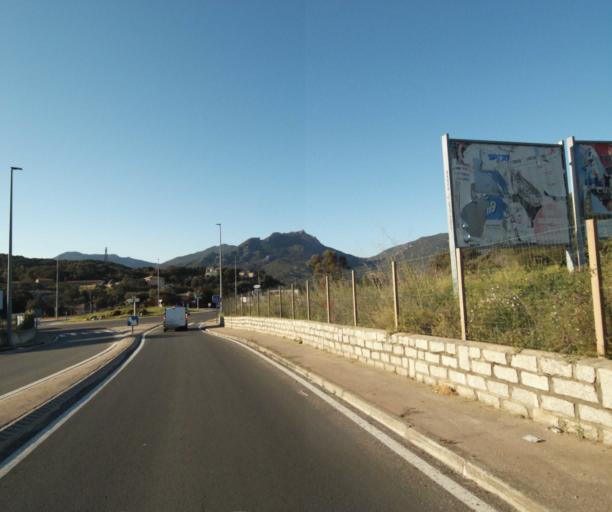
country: FR
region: Corsica
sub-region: Departement de la Corse-du-Sud
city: Propriano
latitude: 41.6681
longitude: 8.9212
